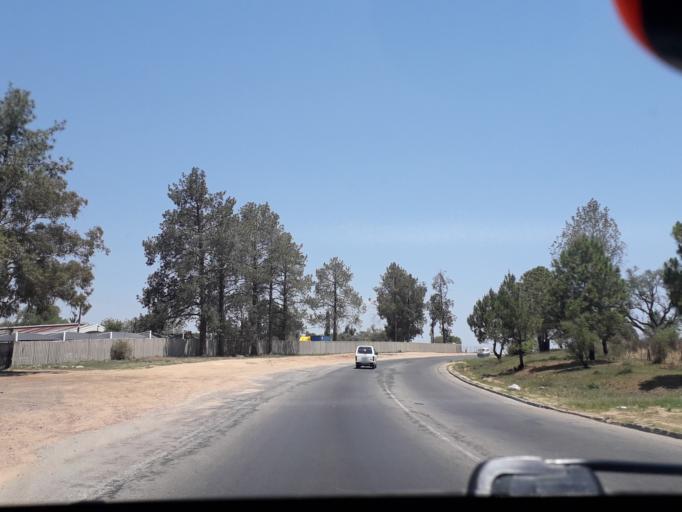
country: ZA
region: Gauteng
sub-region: City of Johannesburg Metropolitan Municipality
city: Midrand
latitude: -26.0324
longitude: 28.1113
